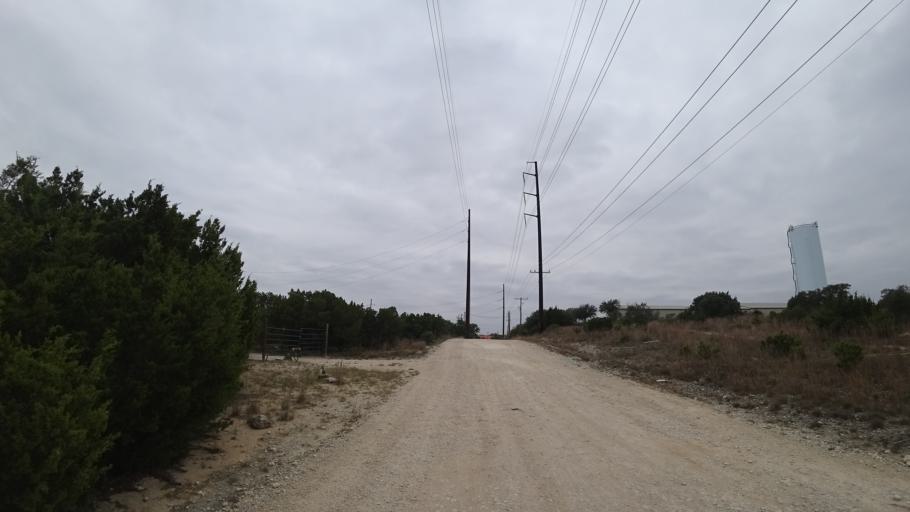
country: US
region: Texas
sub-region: Travis County
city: Lakeway
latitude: 30.3738
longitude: -97.9446
